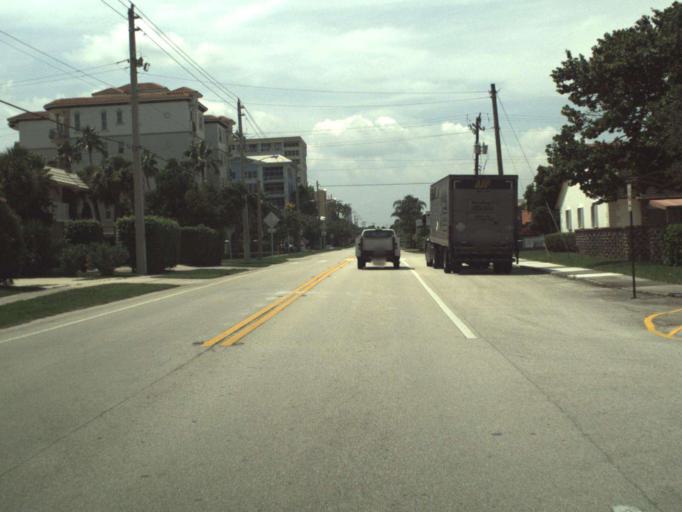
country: US
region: Florida
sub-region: Broward County
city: Hillsboro Beach
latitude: 26.3101
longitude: -80.0777
